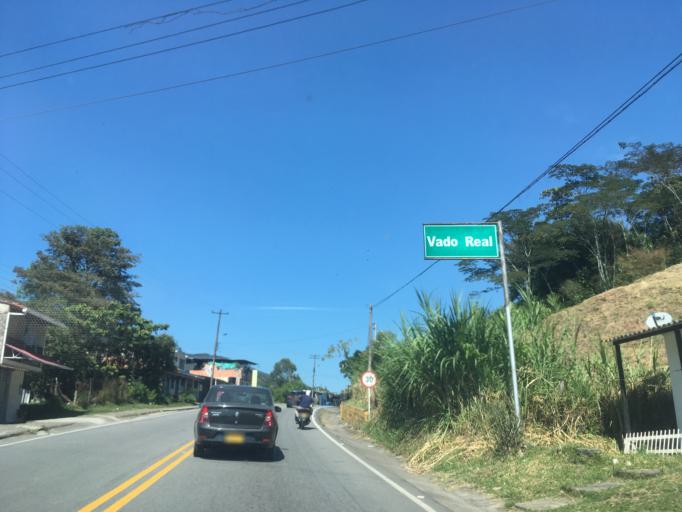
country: CO
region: Santander
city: Suaita
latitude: 6.0672
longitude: -73.4153
